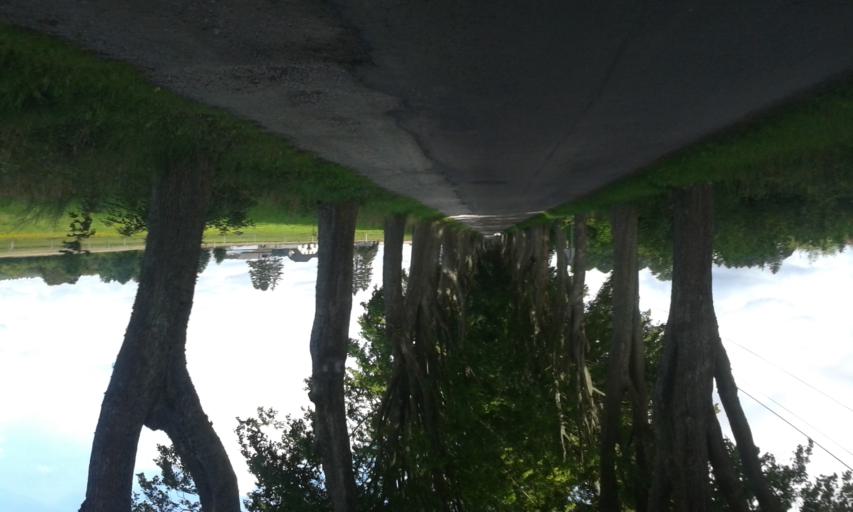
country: PL
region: West Pomeranian Voivodeship
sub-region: Powiat slawienski
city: Slawno
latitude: 54.3104
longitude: 16.6184
